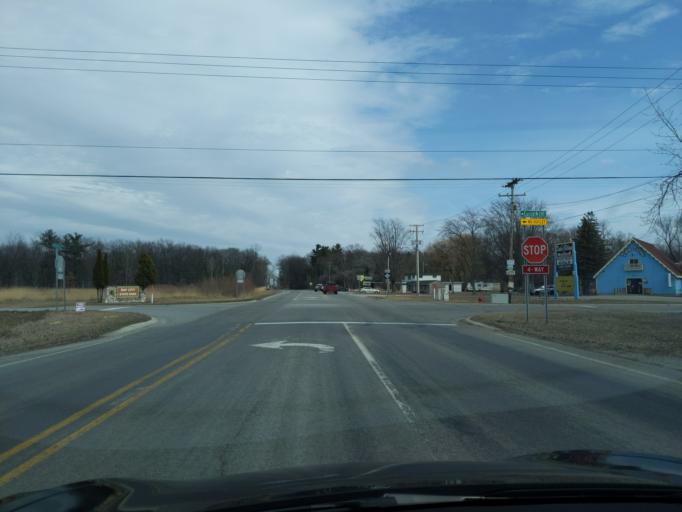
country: US
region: Michigan
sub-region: Bay County
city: Bay City
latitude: 43.6671
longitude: -83.9127
